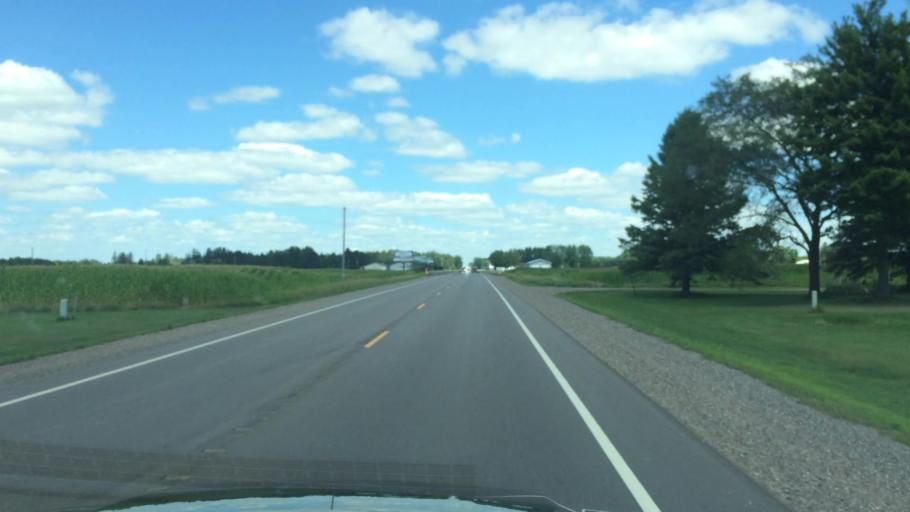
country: US
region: Wisconsin
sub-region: Clark County
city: Abbotsford
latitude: 45.0117
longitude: -90.3153
